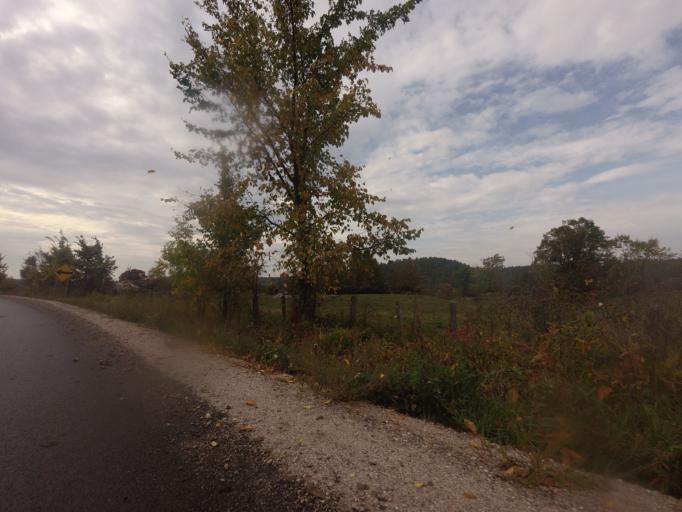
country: CA
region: Quebec
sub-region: Outaouais
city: Wakefield
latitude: 45.9817
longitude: -75.9369
